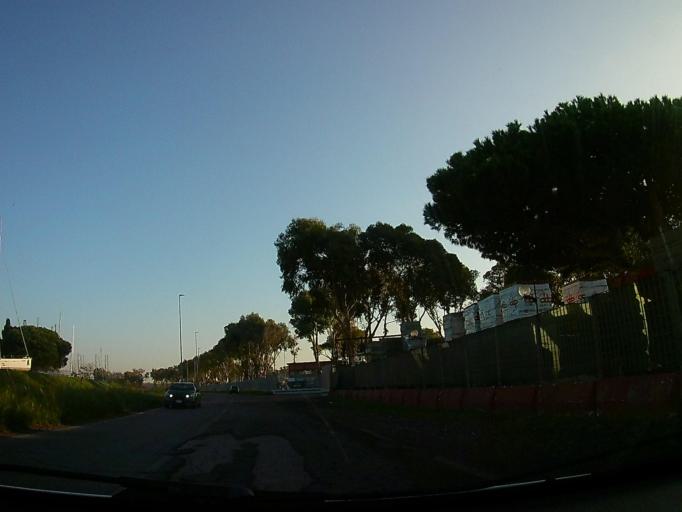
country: IT
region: Latium
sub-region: Citta metropolitana di Roma Capitale
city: Lido di Ostia
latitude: 41.7467
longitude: 12.2693
